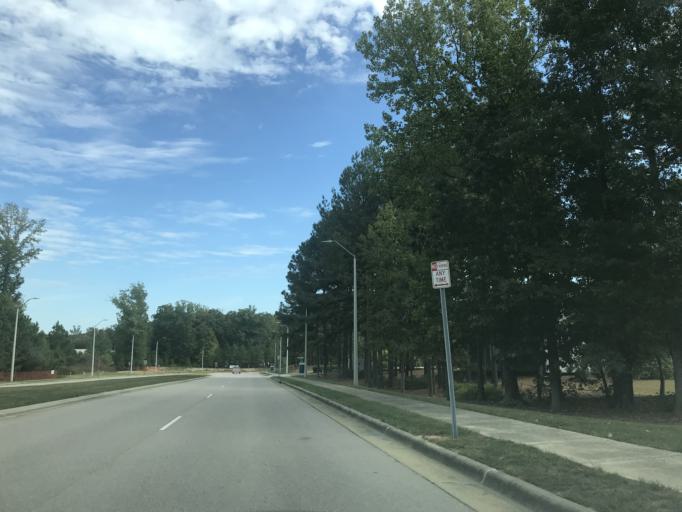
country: US
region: North Carolina
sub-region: Wake County
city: Rolesville
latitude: 35.8689
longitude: -78.5406
